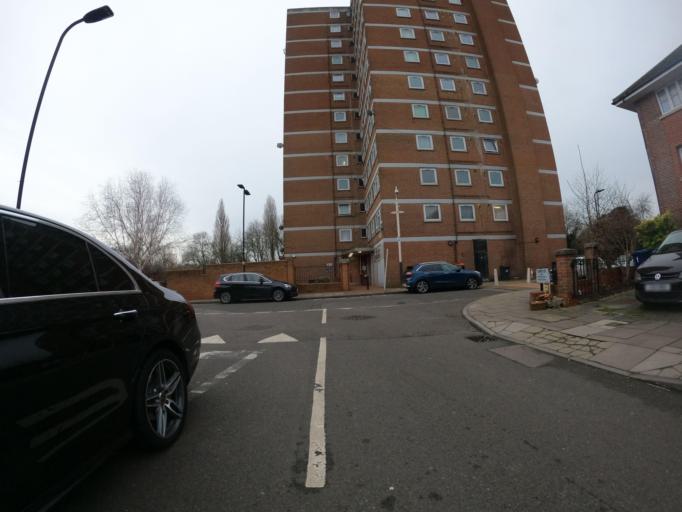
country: GB
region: England
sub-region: Greater London
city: Greenford
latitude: 51.5159
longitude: -0.3593
